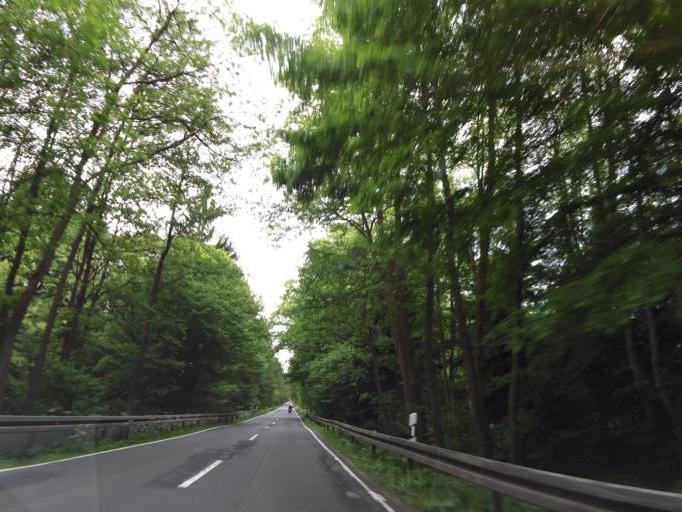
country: DE
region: Hesse
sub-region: Regierungsbezirk Darmstadt
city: Messel
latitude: 49.9599
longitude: 8.7433
